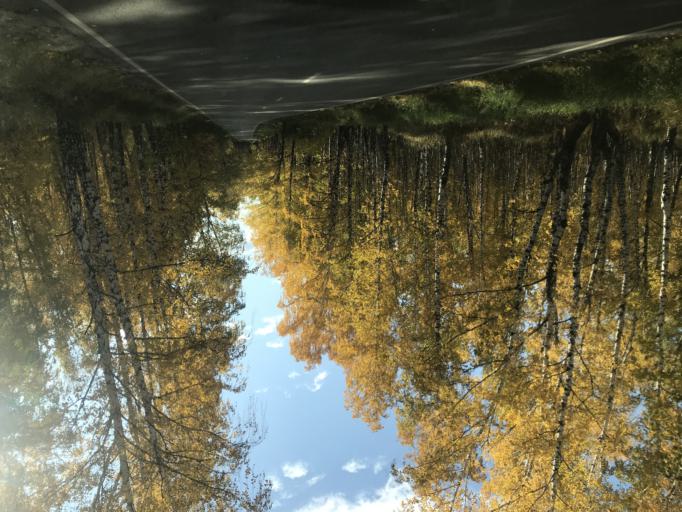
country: RU
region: Chelyabinsk
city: Dolgoderevenskoye
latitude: 55.2745
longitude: 61.3649
